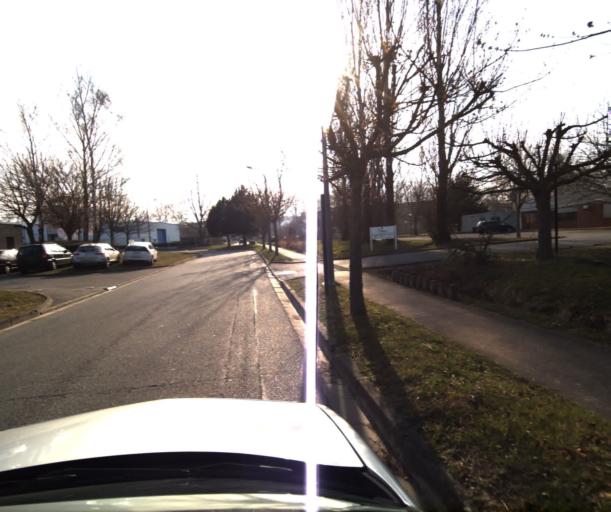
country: FR
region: Midi-Pyrenees
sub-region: Departement de la Haute-Garonne
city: Ramonville-Saint-Agne
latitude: 43.5518
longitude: 1.4845
